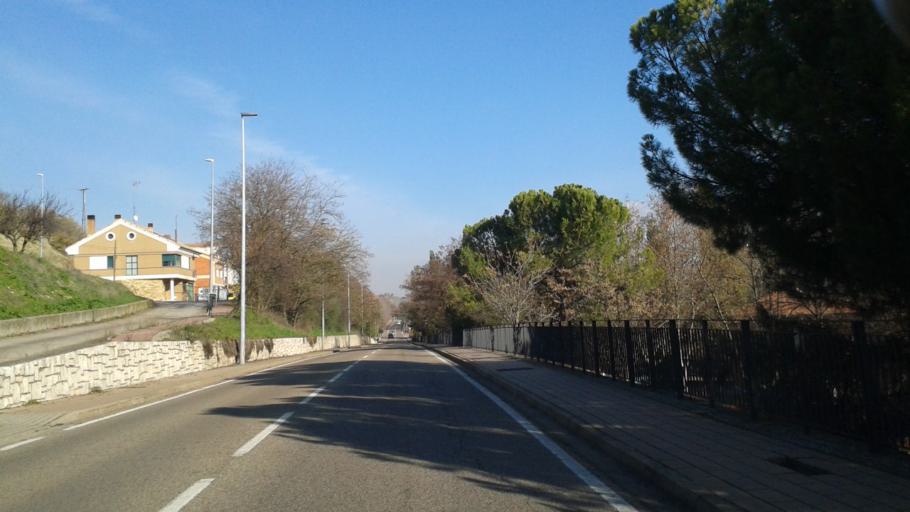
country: ES
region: Castille and Leon
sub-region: Provincia de Valladolid
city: Valladolid
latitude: 41.6651
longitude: -4.7394
